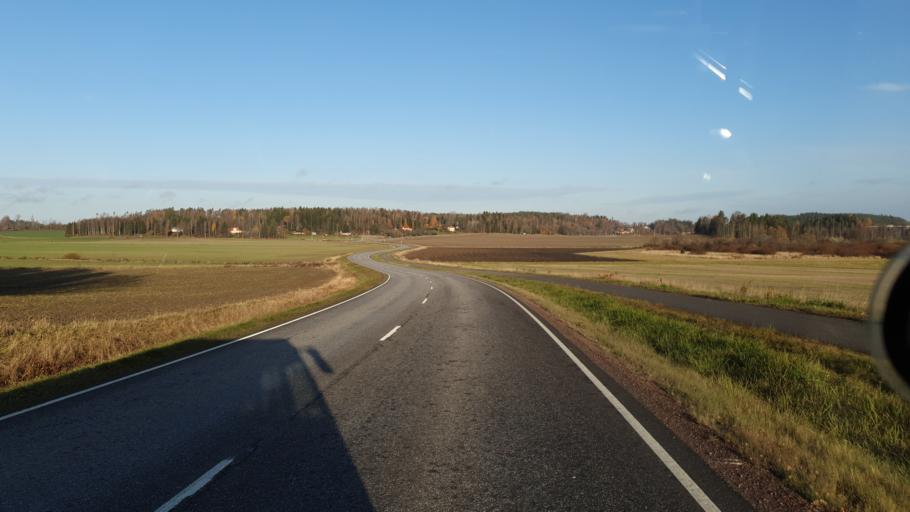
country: FI
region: Uusimaa
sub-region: Helsinki
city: Siuntio
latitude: 60.1582
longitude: 24.2056
